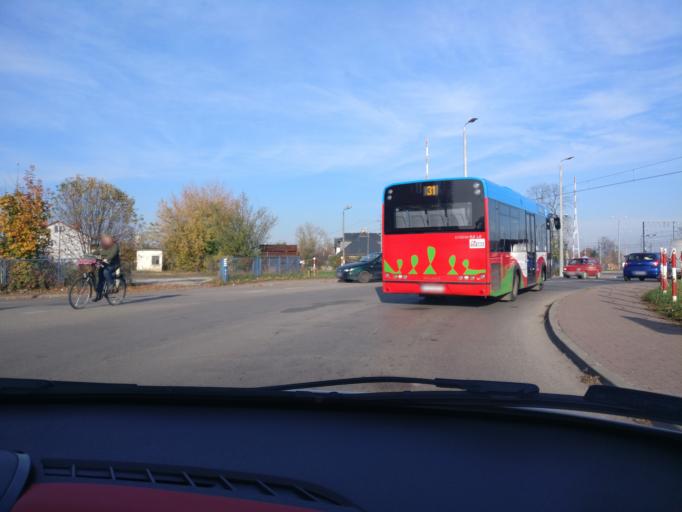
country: PL
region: Lublin Voivodeship
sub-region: Powiat rycki
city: Deblin
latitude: 51.5752
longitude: 21.8377
